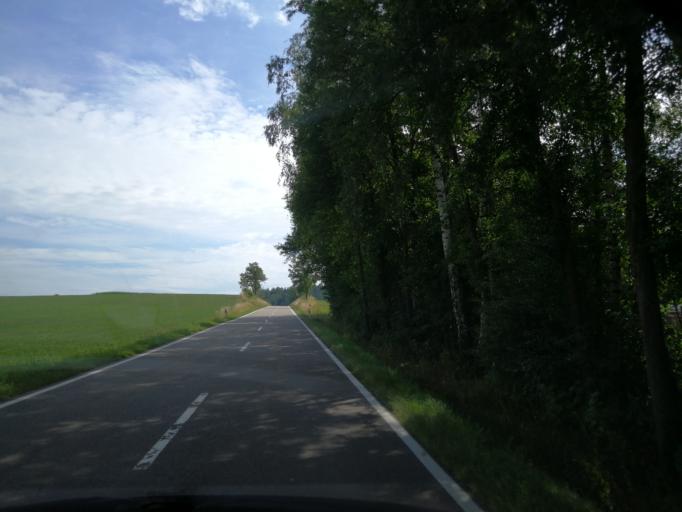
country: DE
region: Bavaria
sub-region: Lower Bavaria
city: Wiesenfelden
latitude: 49.0451
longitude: 12.5490
